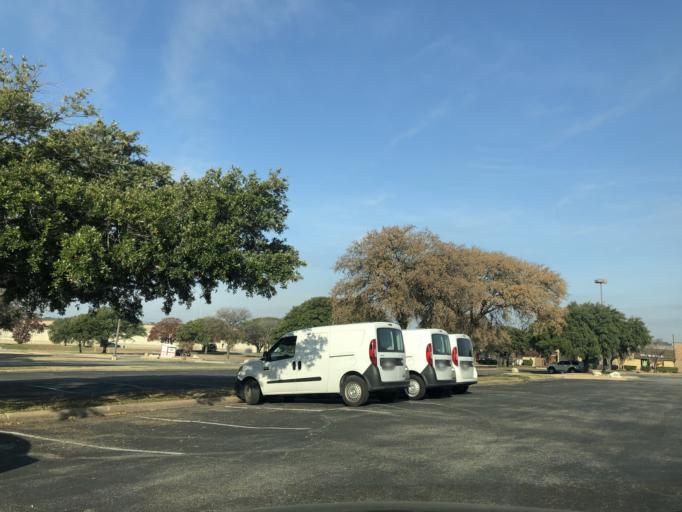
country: US
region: Texas
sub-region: Travis County
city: Wells Branch
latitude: 30.4383
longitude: -97.6965
